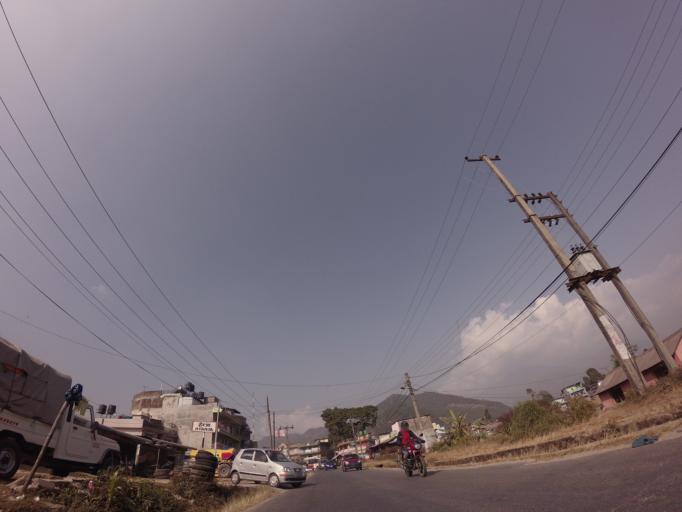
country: NP
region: Western Region
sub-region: Gandaki Zone
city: Pokhara
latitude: 28.2773
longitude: 83.9372
